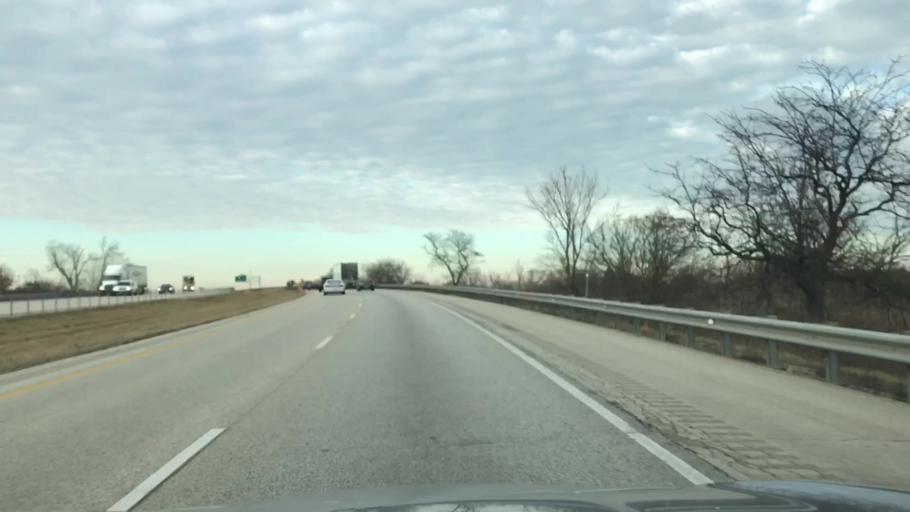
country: US
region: Illinois
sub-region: Sangamon County
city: Sherman
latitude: 39.9006
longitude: -89.5939
